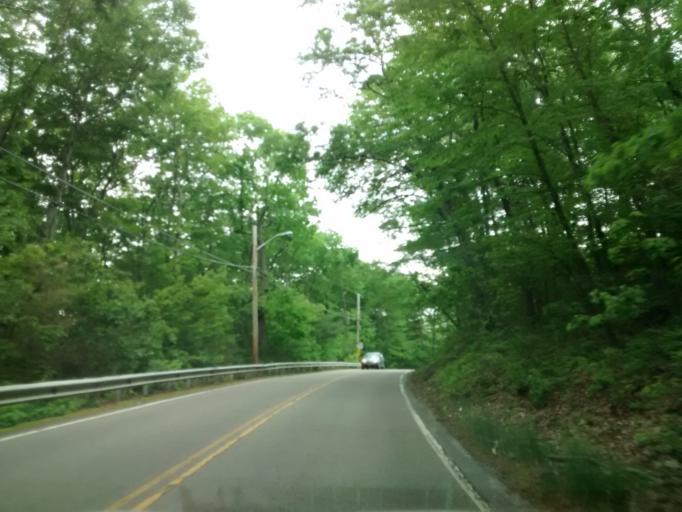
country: US
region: Massachusetts
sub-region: Worcester County
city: Whitinsville
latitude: 42.1212
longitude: -71.6911
